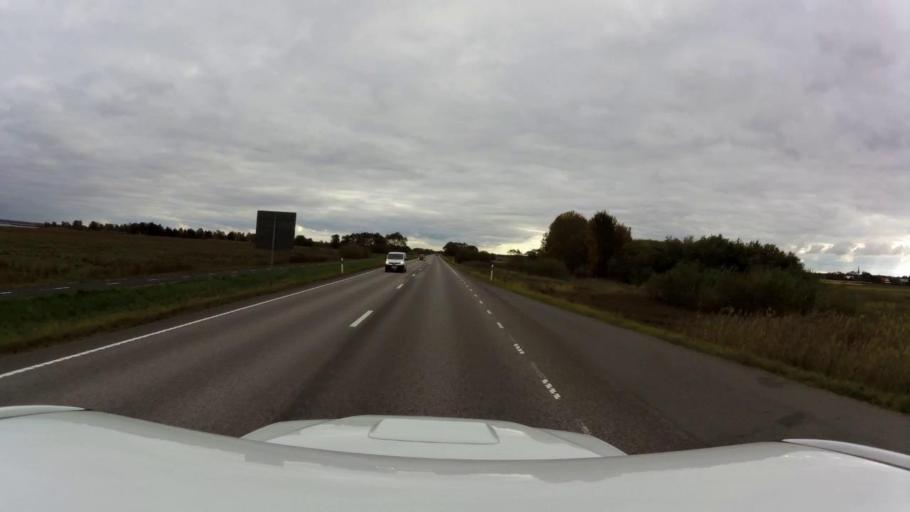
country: SE
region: OEstergoetland
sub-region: Linkopings Kommun
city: Berg
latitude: 58.4653
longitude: 15.5353
